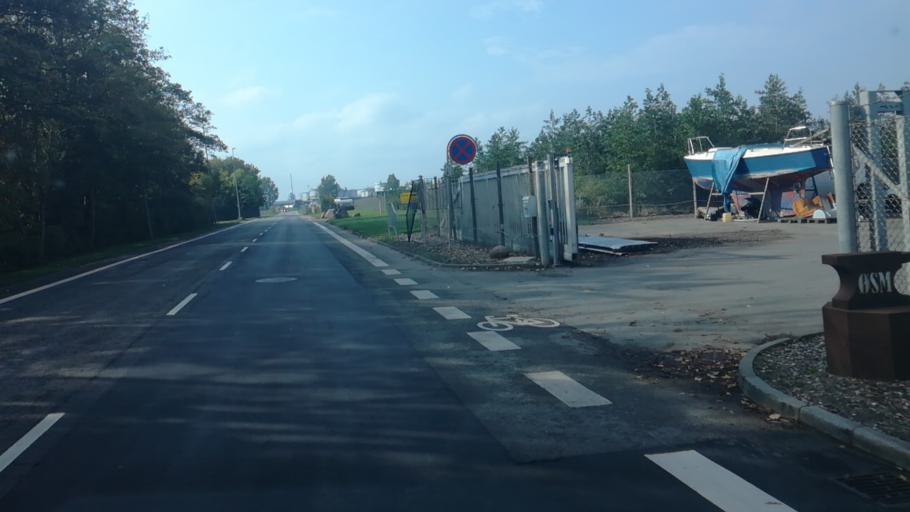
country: DK
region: South Denmark
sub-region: Fredericia Kommune
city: Fredericia
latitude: 55.5930
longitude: 9.7629
